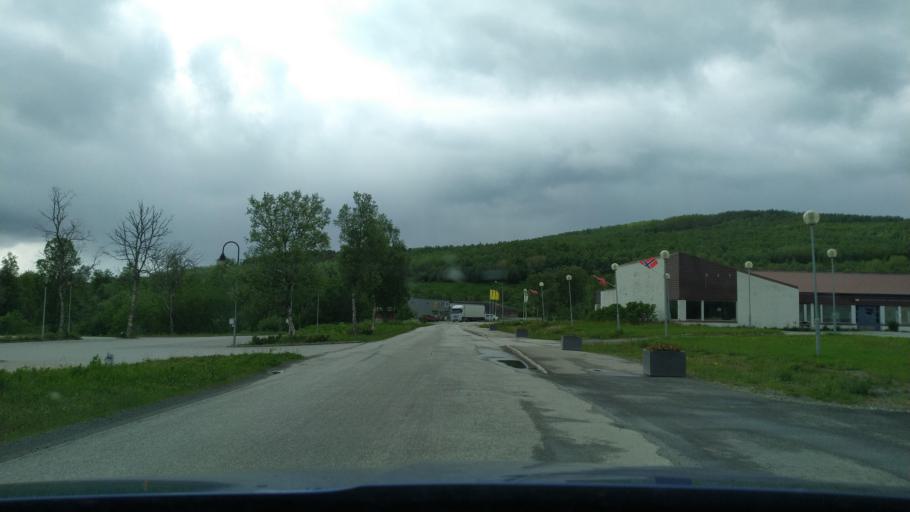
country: NO
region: Troms
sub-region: Dyroy
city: Brostadbotn
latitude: 69.0905
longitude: 17.6990
